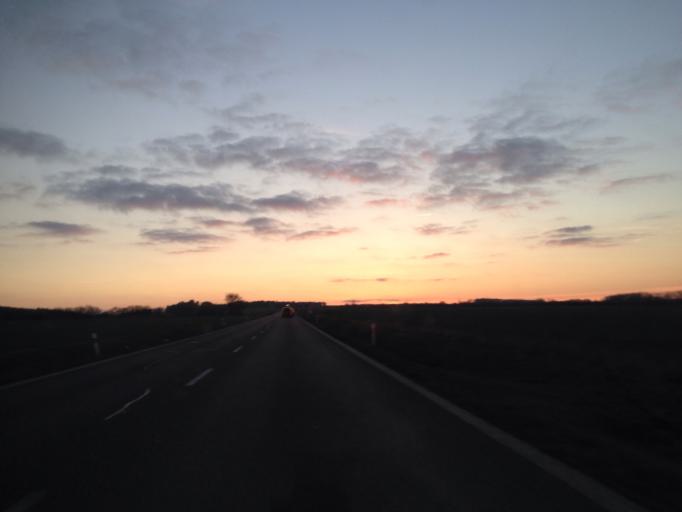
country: CZ
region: Central Bohemia
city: Rakovnik
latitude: 50.1706
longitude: 13.7048
